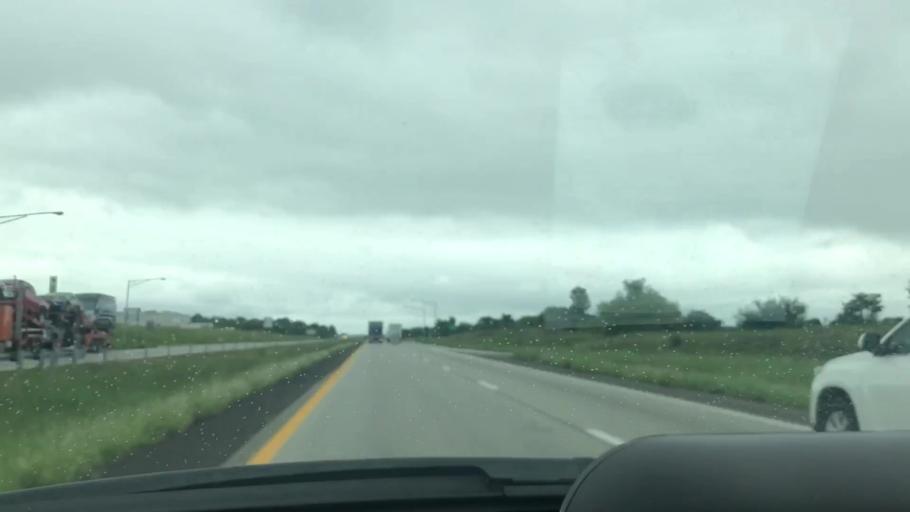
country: US
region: Missouri
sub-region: Greene County
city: Republic
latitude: 37.2012
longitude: -93.4222
